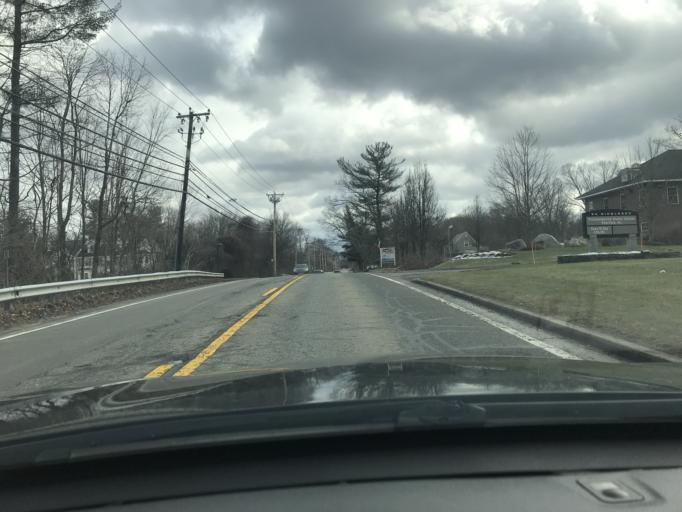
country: US
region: Massachusetts
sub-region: Middlesex County
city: Tyngsboro
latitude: 42.6636
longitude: -71.4095
